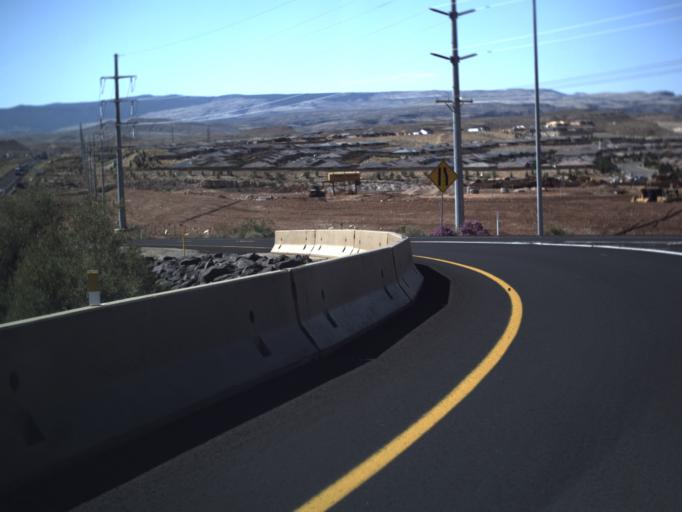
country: US
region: Utah
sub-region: Washington County
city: Saint George
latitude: 37.0276
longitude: -113.6059
